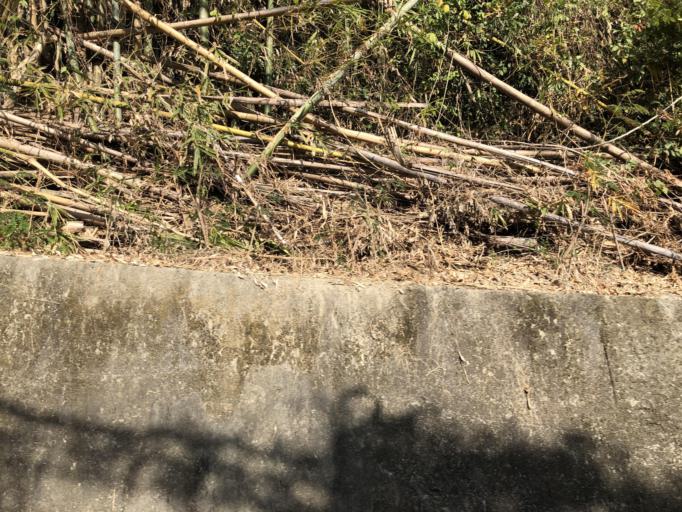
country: TW
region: Taiwan
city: Yujing
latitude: 23.0099
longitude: 120.3988
